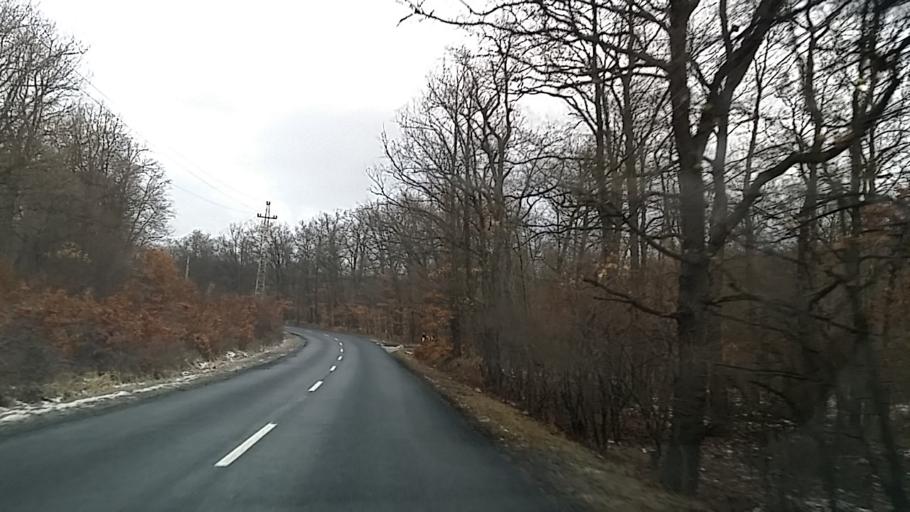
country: HU
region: Pest
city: Nagykovacsi
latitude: 47.7096
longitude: 19.0163
